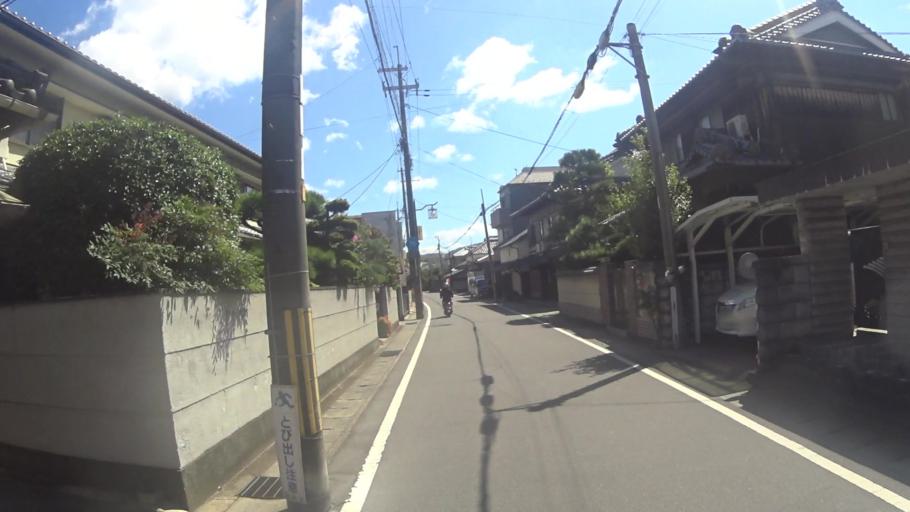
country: JP
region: Nara
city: Nara-shi
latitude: 34.7198
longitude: 135.8844
